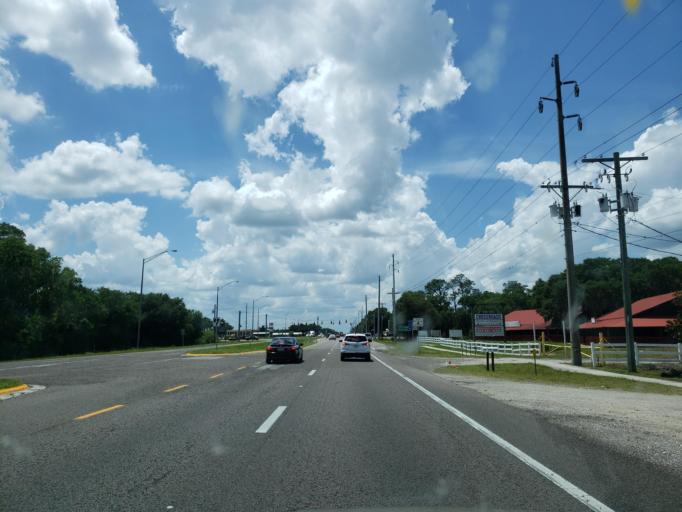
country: US
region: Florida
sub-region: Hillsborough County
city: Plant City
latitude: 27.9378
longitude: -82.1186
